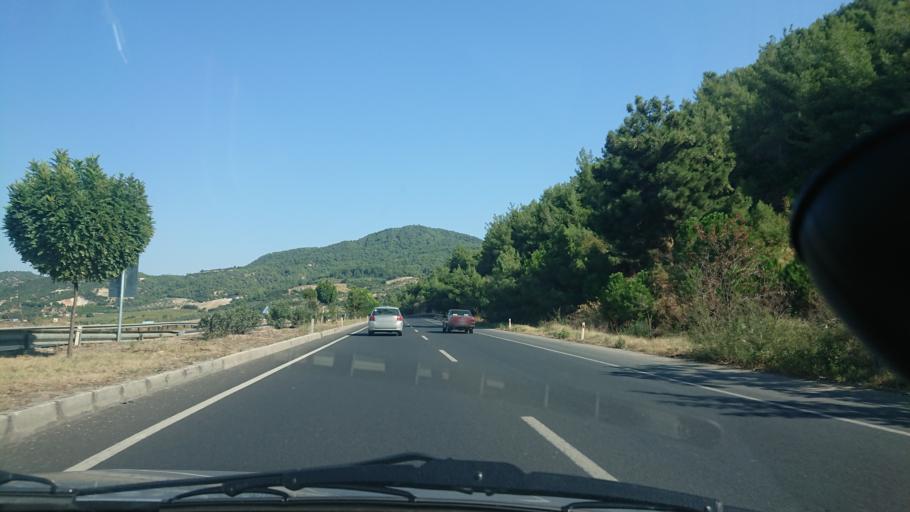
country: TR
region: Manisa
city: Turgutlu
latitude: 38.4838
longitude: 27.8125
